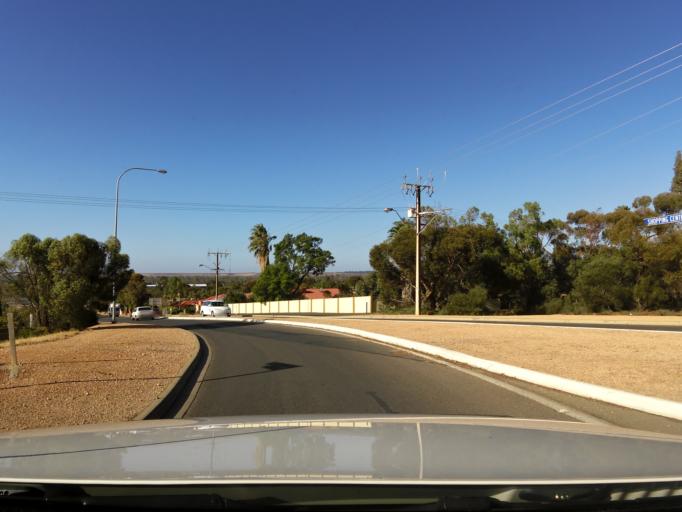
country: AU
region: South Australia
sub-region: Berri and Barmera
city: Berri
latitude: -34.2727
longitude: 140.6070
